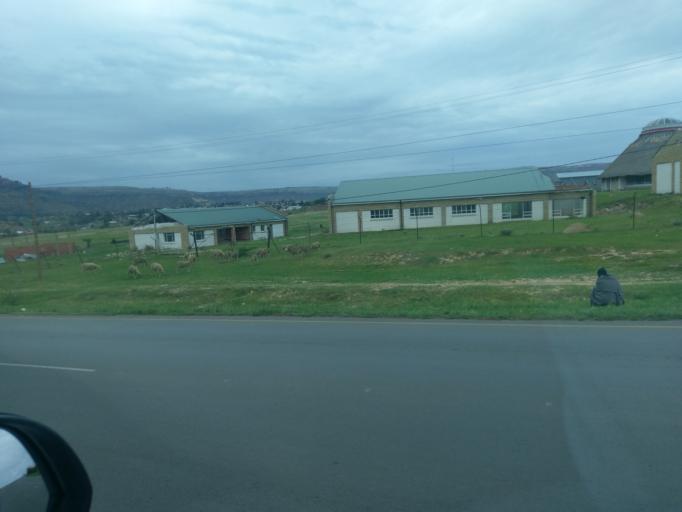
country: LS
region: Maseru
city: Maseru
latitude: -29.2653
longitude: 27.5442
